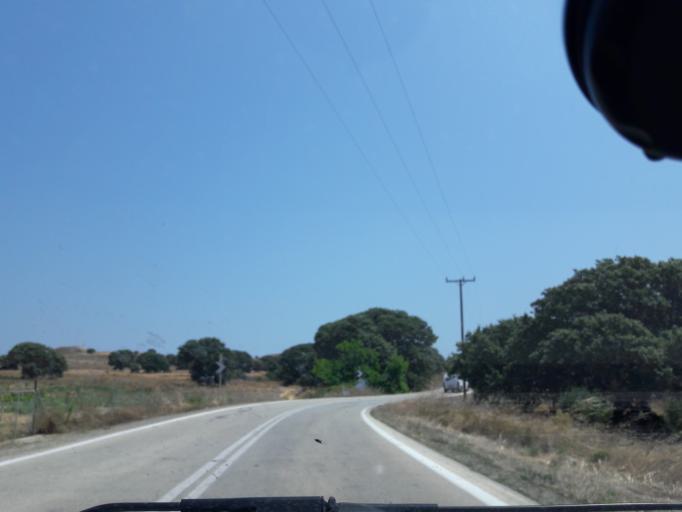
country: GR
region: North Aegean
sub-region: Nomos Lesvou
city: Myrina
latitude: 39.9248
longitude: 25.3175
